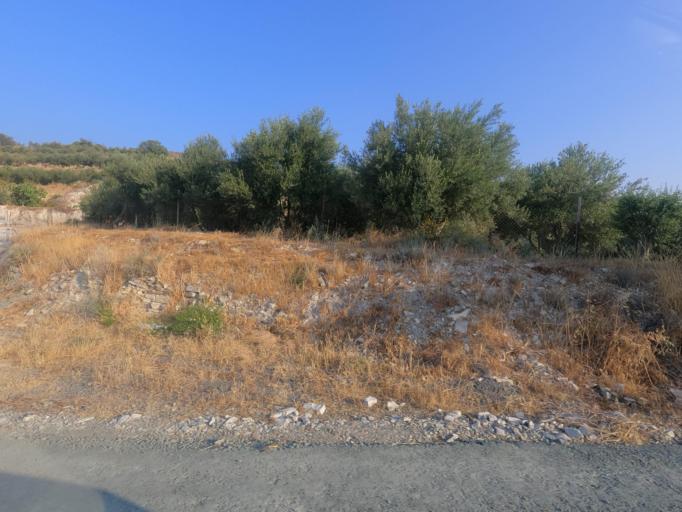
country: CY
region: Larnaka
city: Psevdas
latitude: 34.9379
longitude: 33.5037
